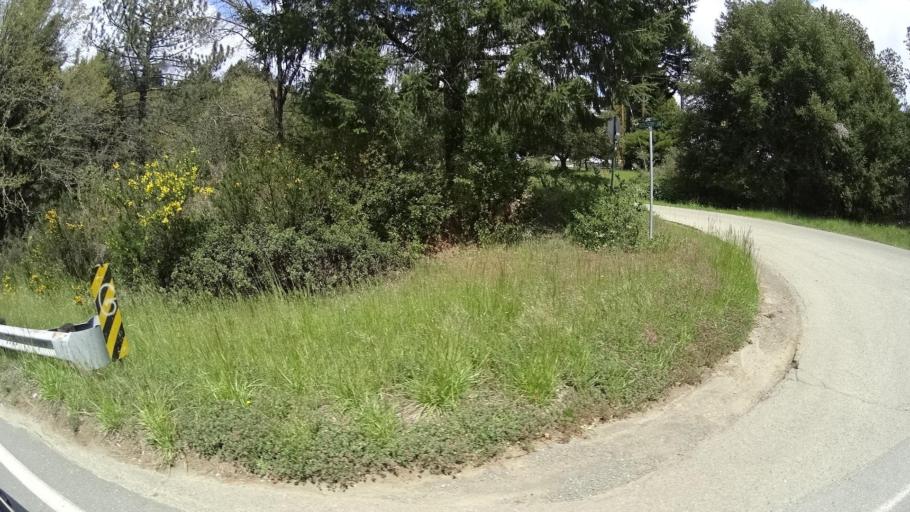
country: US
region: California
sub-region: Humboldt County
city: Redway
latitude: 40.0583
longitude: -123.9730
